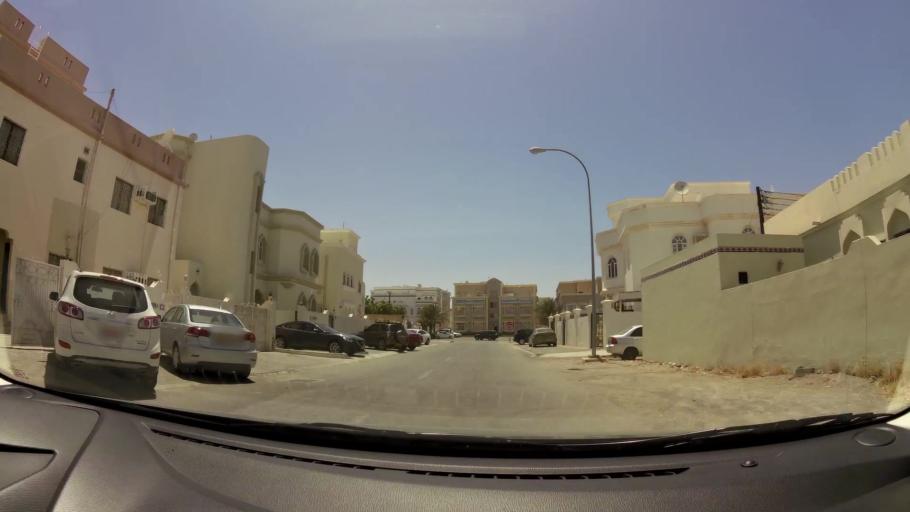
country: OM
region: Muhafazat Masqat
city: Bawshar
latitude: 23.5925
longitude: 58.3786
